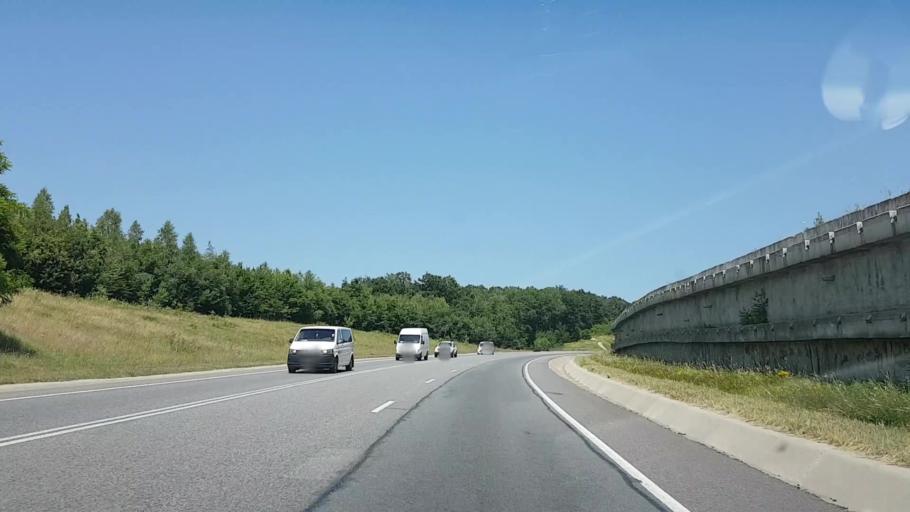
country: RO
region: Cluj
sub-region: Comuna Feleacu
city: Feleacu
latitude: 46.7082
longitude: 23.6443
